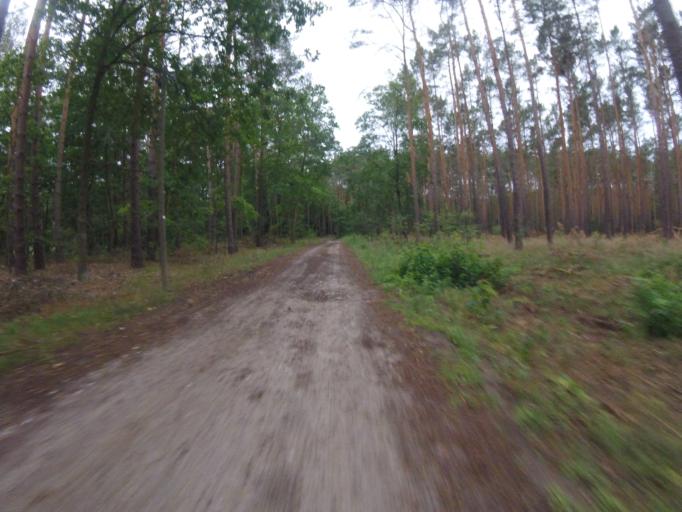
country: DE
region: Brandenburg
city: Bestensee
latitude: 52.2297
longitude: 13.7189
